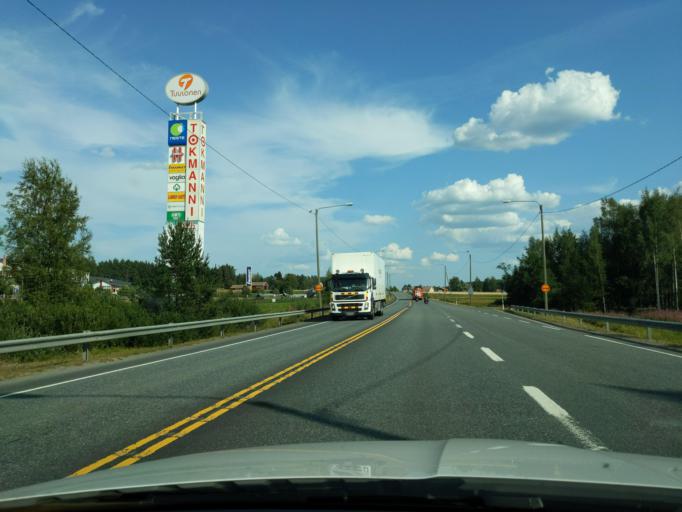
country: FI
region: Haeme
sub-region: Haemeenlinna
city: Tuulos
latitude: 61.1044
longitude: 24.8612
